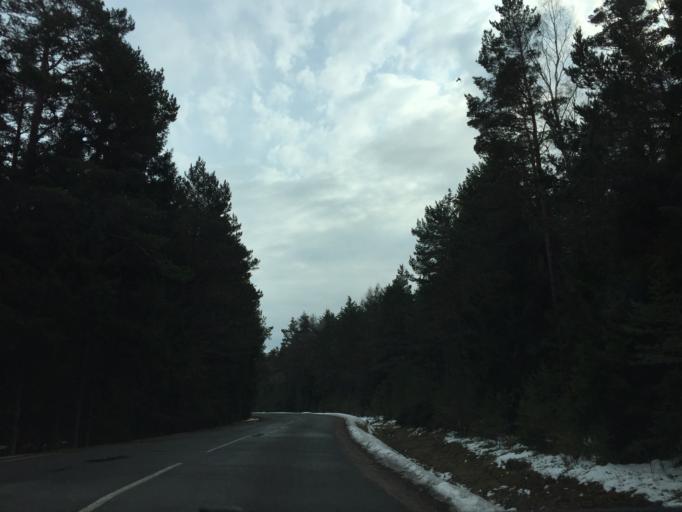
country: EE
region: Saare
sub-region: Kuressaare linn
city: Kuressaare
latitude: 58.4542
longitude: 22.0490
